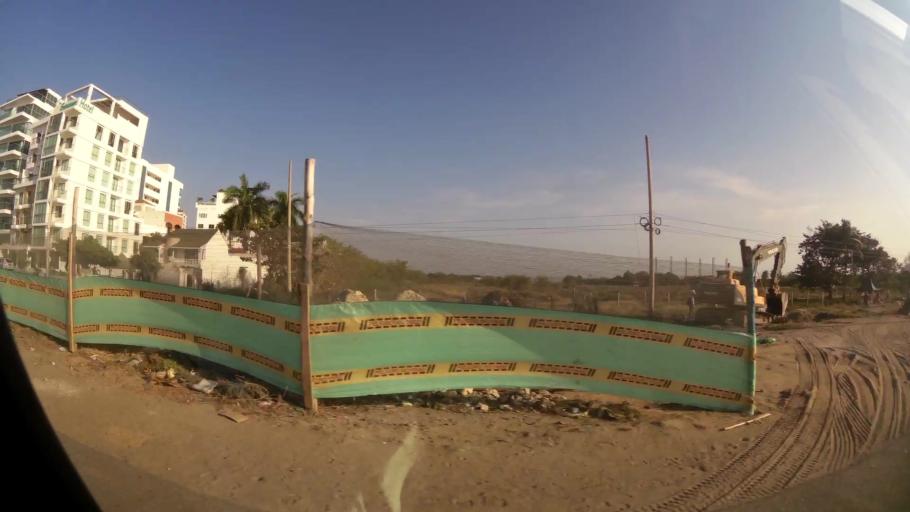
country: CO
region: Bolivar
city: Cartagena
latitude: 10.4570
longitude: -75.5097
